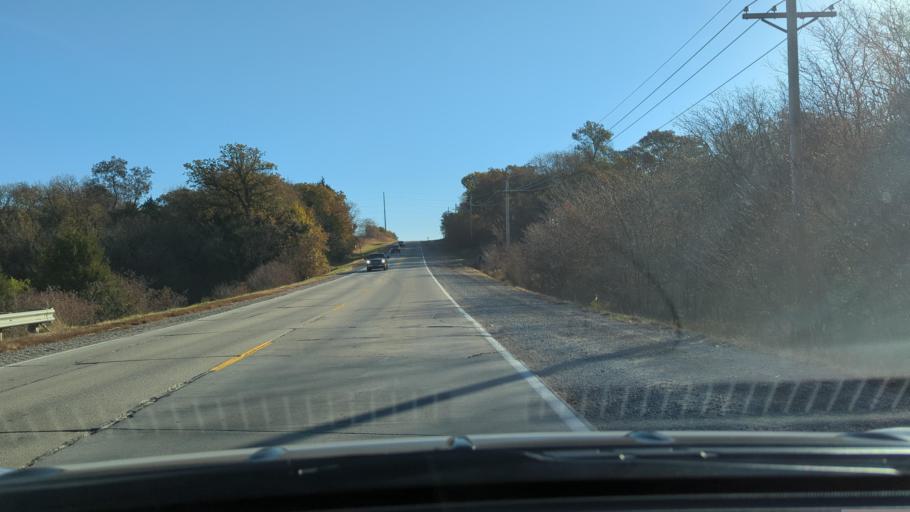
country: US
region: Nebraska
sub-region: Sarpy County
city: Offutt Air Force Base
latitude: 41.0926
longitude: -95.9908
